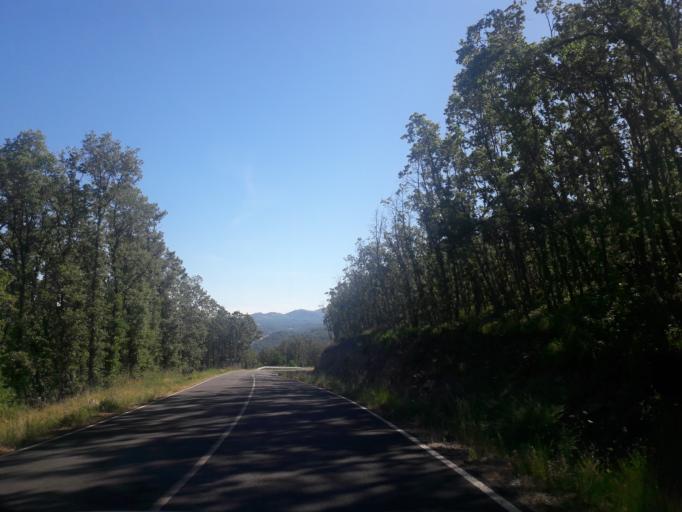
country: ES
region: Castille and Leon
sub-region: Provincia de Salamanca
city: Montemayor del Rio
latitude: 40.3414
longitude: -5.8798
